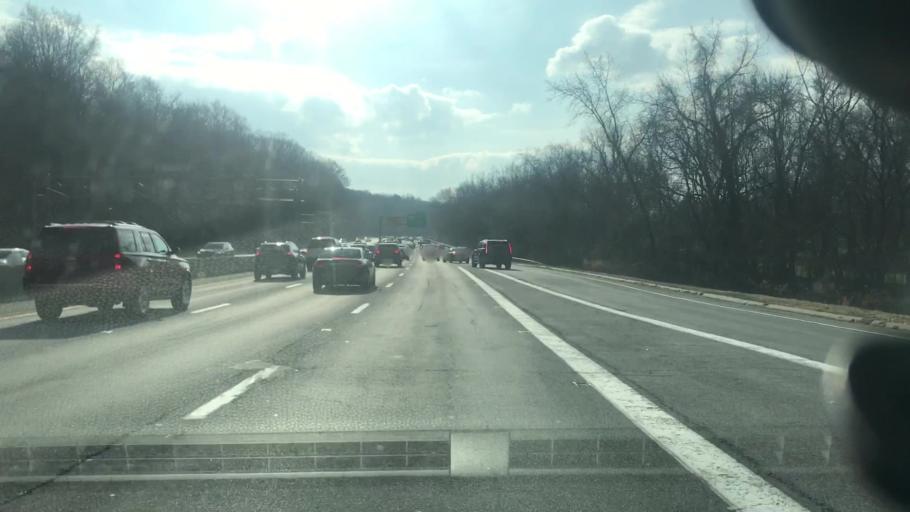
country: US
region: New York
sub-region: Westchester County
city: Purchase
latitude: 41.0103
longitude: -73.7188
